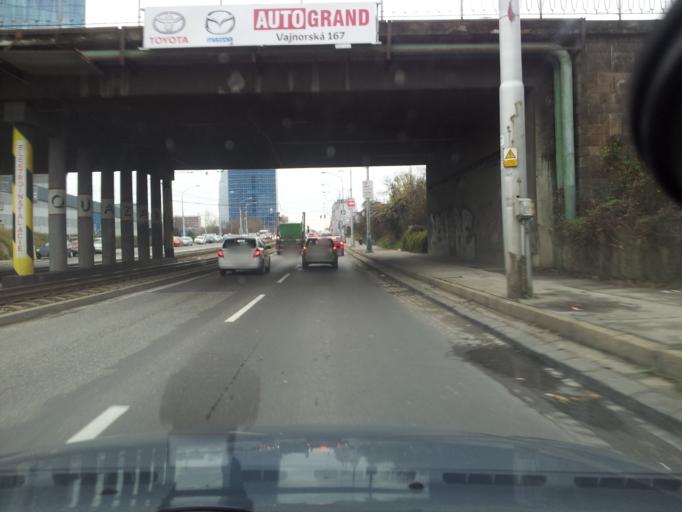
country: SK
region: Bratislavsky
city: Bratislava
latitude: 48.1739
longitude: 17.1431
